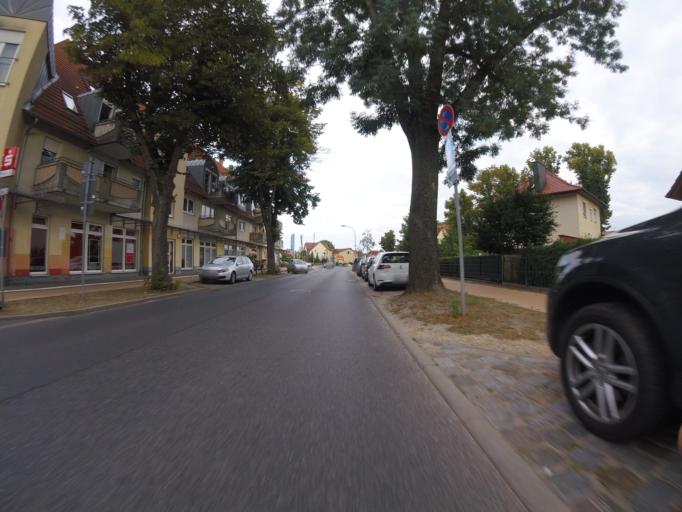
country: DE
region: Brandenburg
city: Birkenwerder
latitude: 52.6727
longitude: 13.3176
